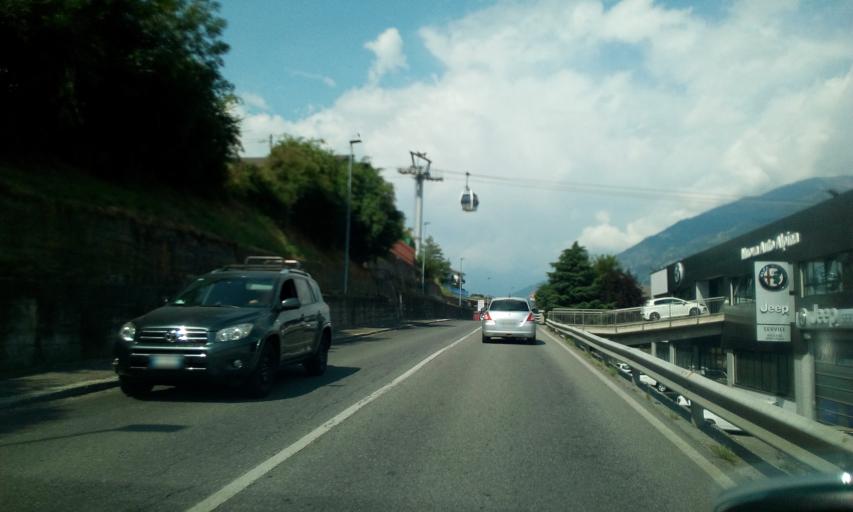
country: IT
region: Aosta Valley
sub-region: Valle d'Aosta
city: Charvensod
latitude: 45.7281
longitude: 7.3193
